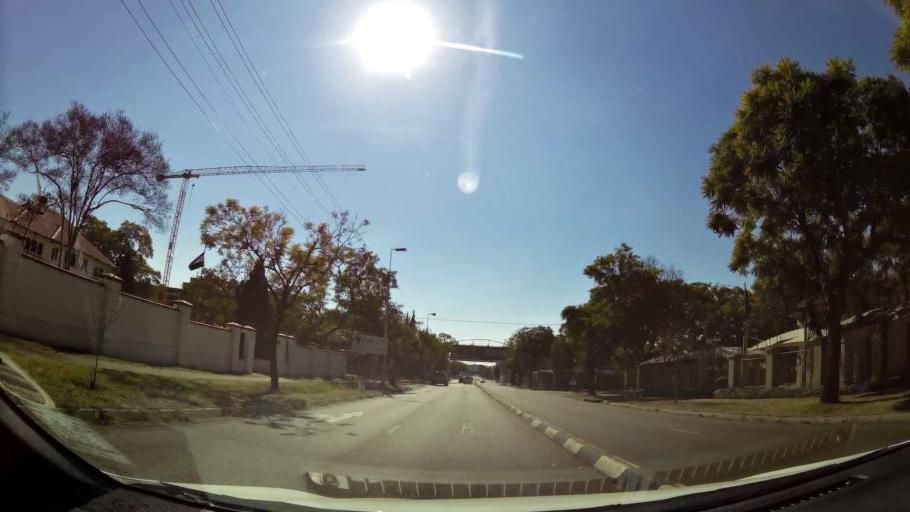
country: ZA
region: Gauteng
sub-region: City of Tshwane Metropolitan Municipality
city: Pretoria
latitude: -25.7601
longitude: 28.2380
